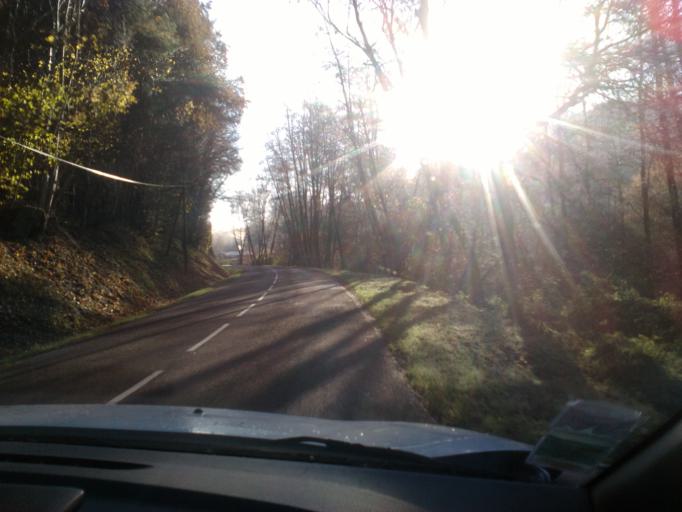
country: FR
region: Lorraine
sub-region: Departement des Vosges
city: Uzemain
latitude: 48.0621
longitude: 6.3339
